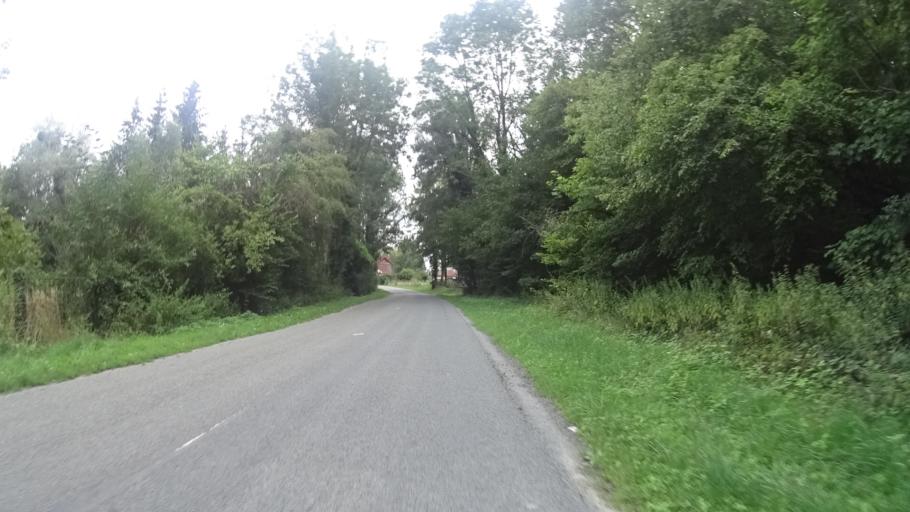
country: FR
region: Picardie
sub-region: Departement de l'Aisne
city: Guise
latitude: 49.8962
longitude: 3.5599
